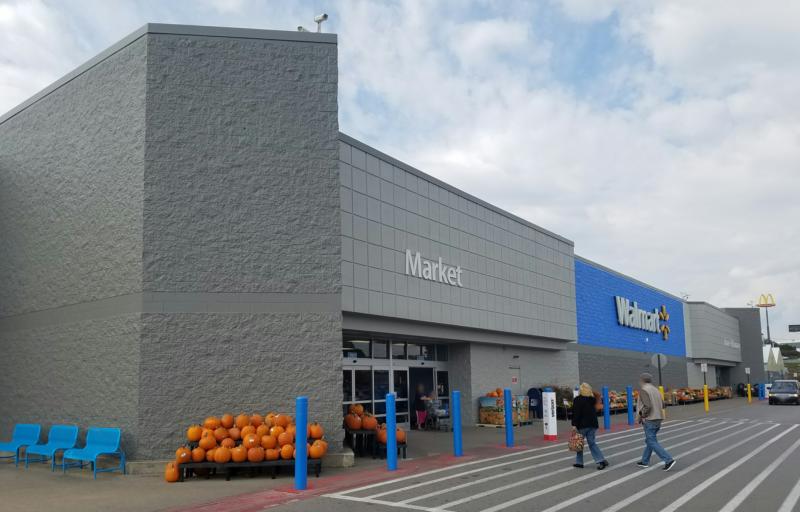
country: US
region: Pennsylvania
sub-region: Clarion County
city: Clarion
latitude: 41.1887
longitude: -79.3962
